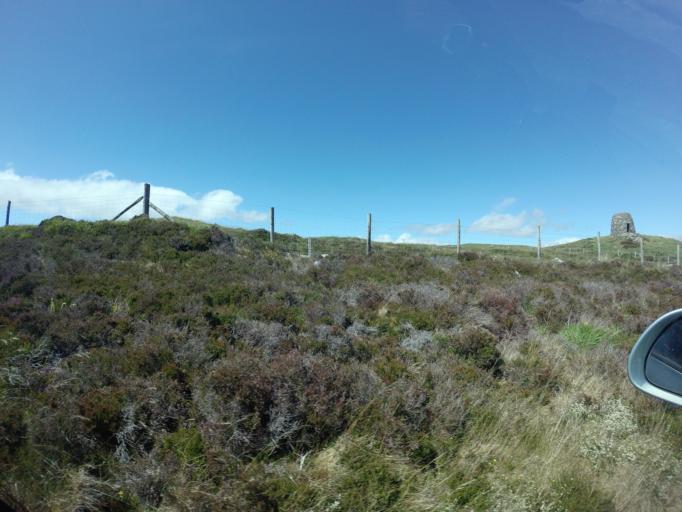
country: GB
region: Scotland
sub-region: Eilean Siar
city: Harris
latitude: 58.0794
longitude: -6.6486
